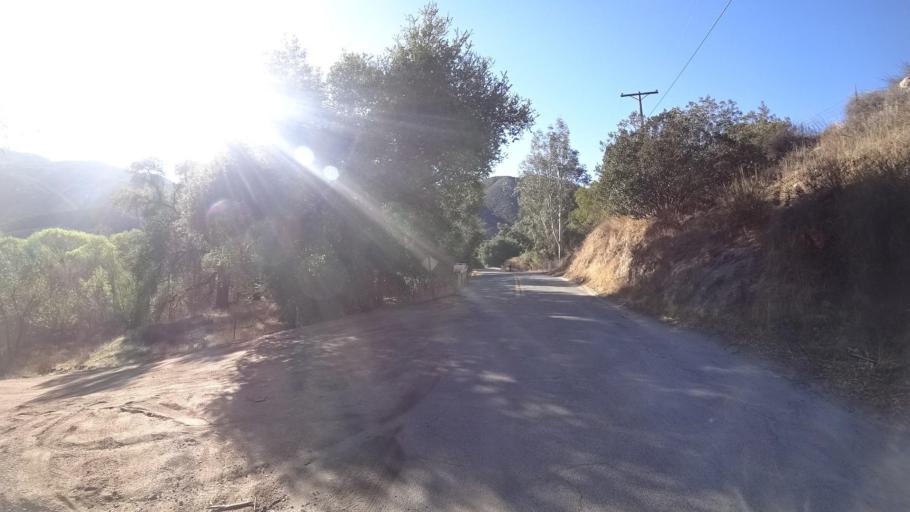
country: MX
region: Baja California
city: Tecate
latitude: 32.6301
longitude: -116.6867
